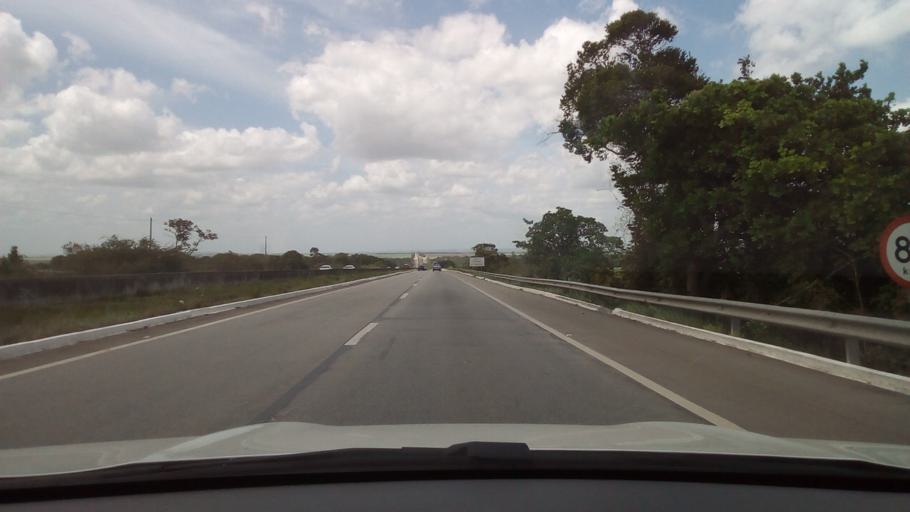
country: BR
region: Paraiba
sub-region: Mamanguape
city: Mamanguape
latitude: -6.9580
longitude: -35.0884
